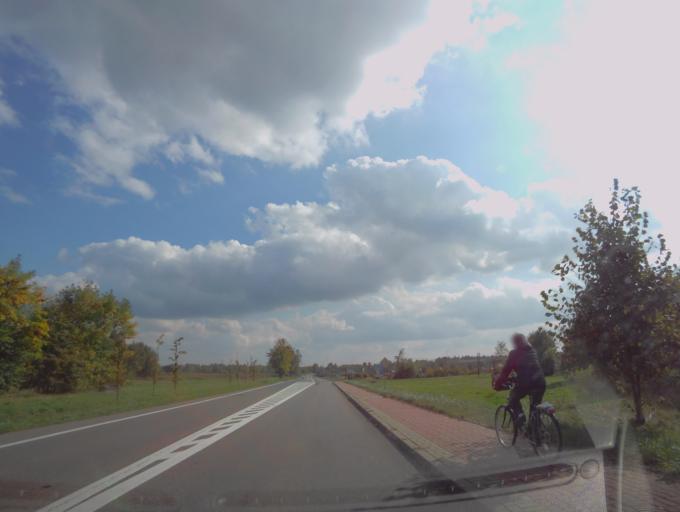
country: PL
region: Lublin Voivodeship
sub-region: Powiat bilgorajski
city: Frampol
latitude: 50.6638
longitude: 22.6744
